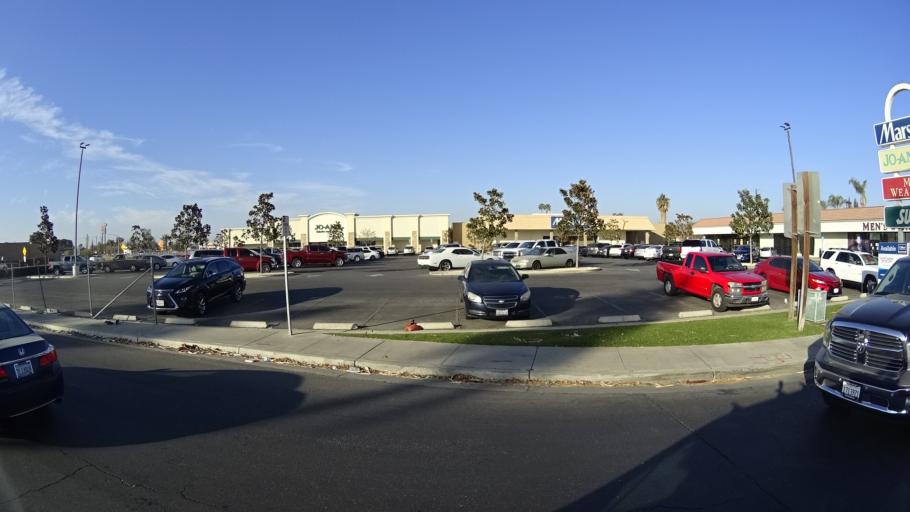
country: US
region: California
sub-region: Kern County
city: Bakersfield
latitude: 35.3396
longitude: -119.0357
